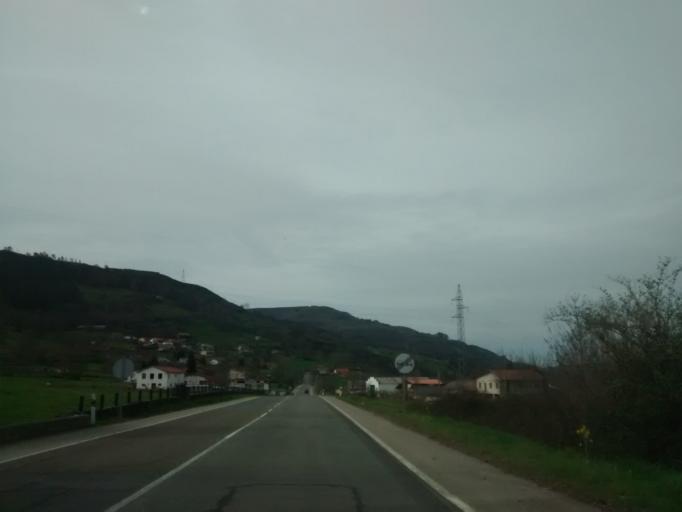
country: ES
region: Cantabria
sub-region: Provincia de Cantabria
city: Santiurde de Toranzo
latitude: 43.2171
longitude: -3.9422
